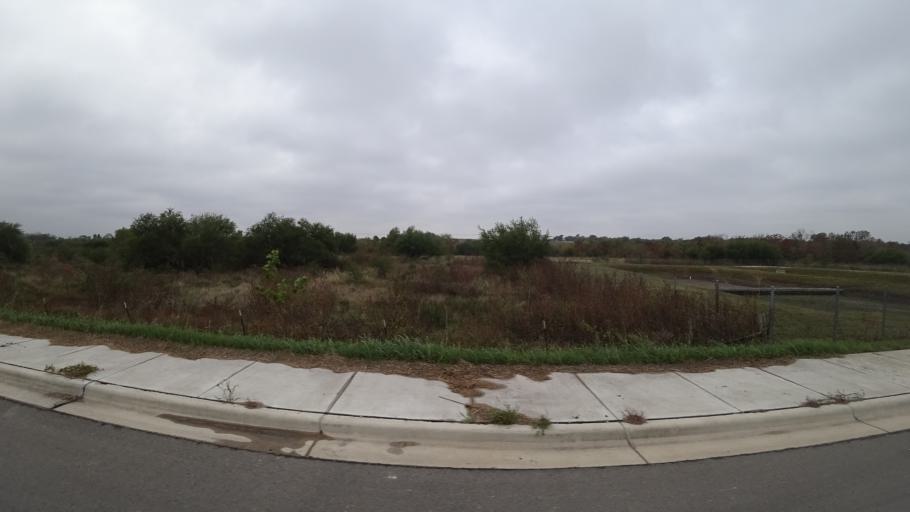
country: US
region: Texas
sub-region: Travis County
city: Pflugerville
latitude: 30.4204
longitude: -97.6174
